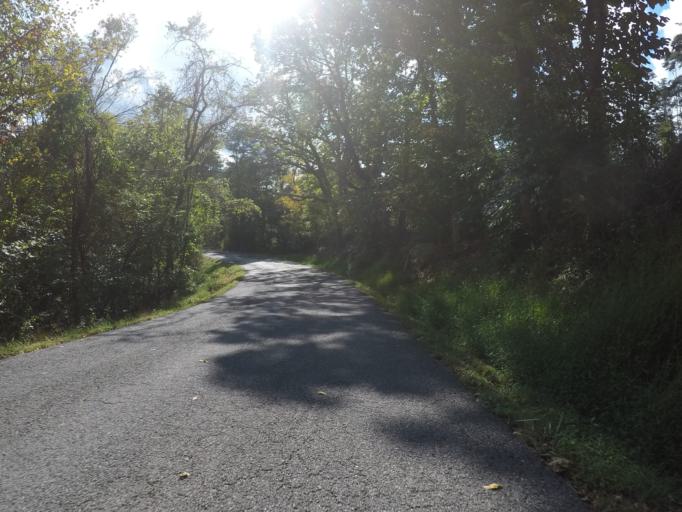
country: US
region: West Virginia
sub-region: Wayne County
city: Lavalette
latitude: 38.3639
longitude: -82.4631
